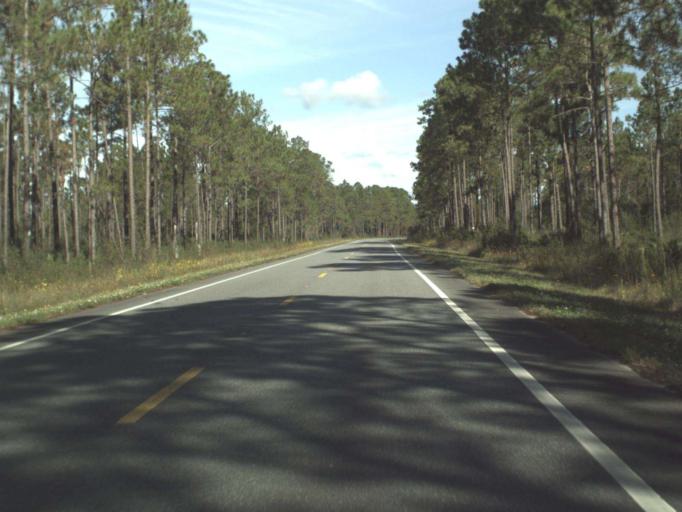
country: US
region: Florida
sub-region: Franklin County
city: Apalachicola
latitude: 29.8936
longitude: -84.9777
